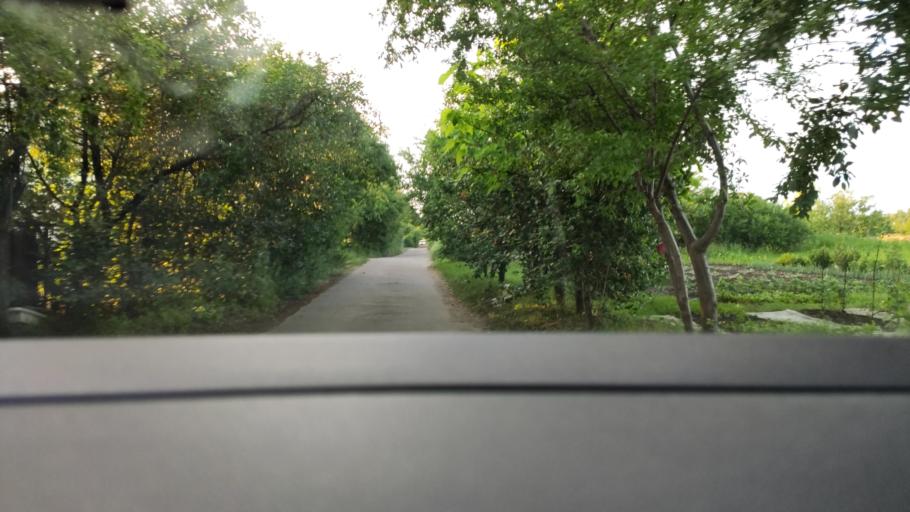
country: RU
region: Voronezj
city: Ramon'
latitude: 51.9096
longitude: 39.1769
